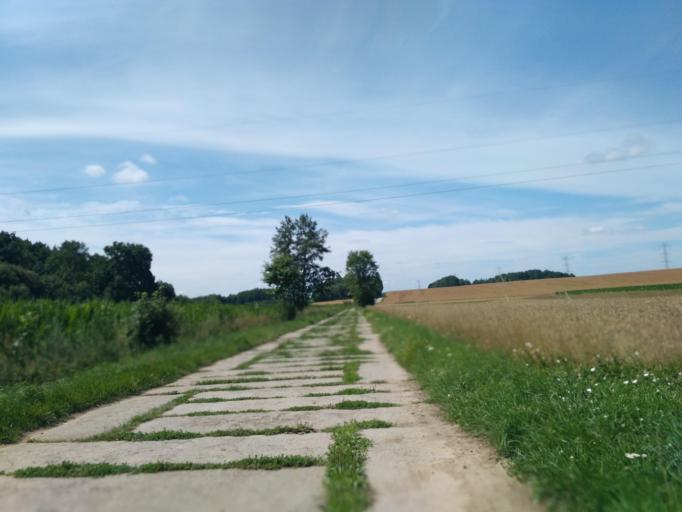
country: PL
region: Subcarpathian Voivodeship
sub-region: Powiat brzozowski
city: Haczow
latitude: 49.6591
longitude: 21.8769
